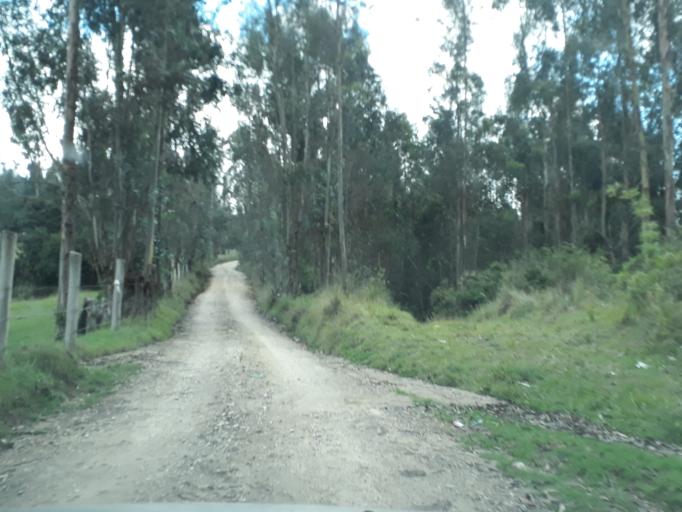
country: CO
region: Cundinamarca
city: Lenguazaque
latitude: 5.2640
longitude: -73.6978
